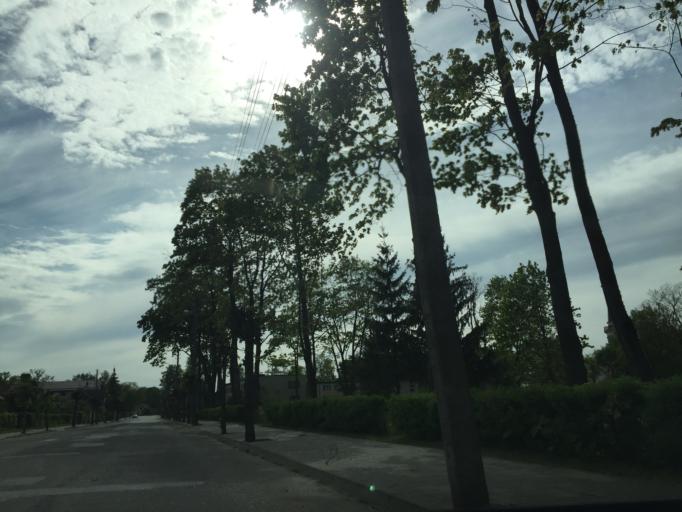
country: LT
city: Linkuva
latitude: 56.0252
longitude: 24.1729
